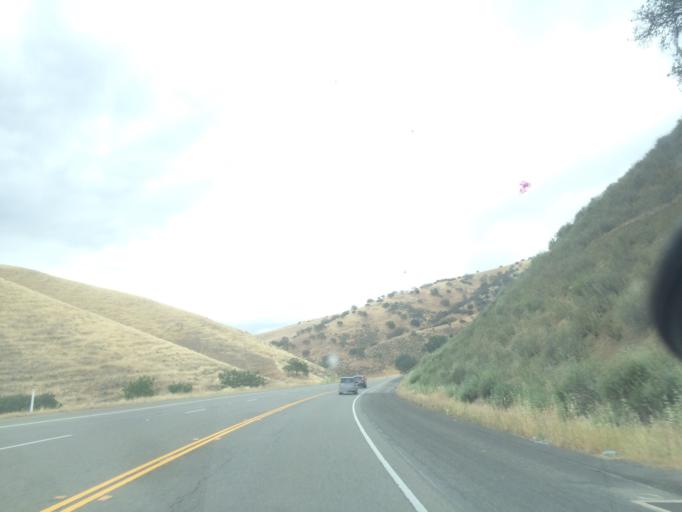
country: US
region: California
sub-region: San Luis Obispo County
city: Shandon
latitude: 35.7764
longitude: -120.1831
